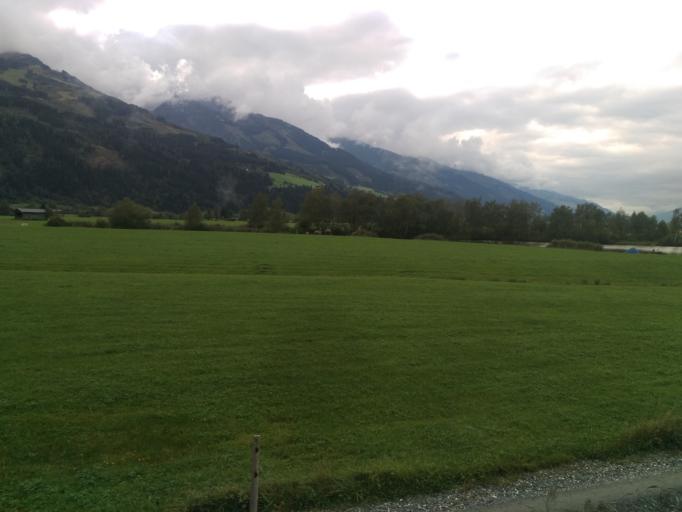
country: AT
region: Salzburg
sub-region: Politischer Bezirk Zell am See
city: Kaprun
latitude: 47.2883
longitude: 12.7423
